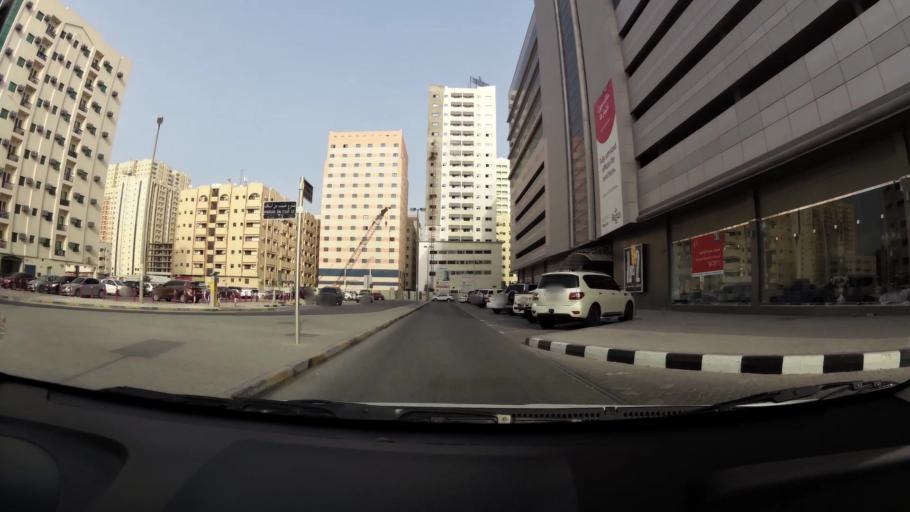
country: AE
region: Ash Shariqah
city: Sharjah
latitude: 25.3434
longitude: 55.3984
